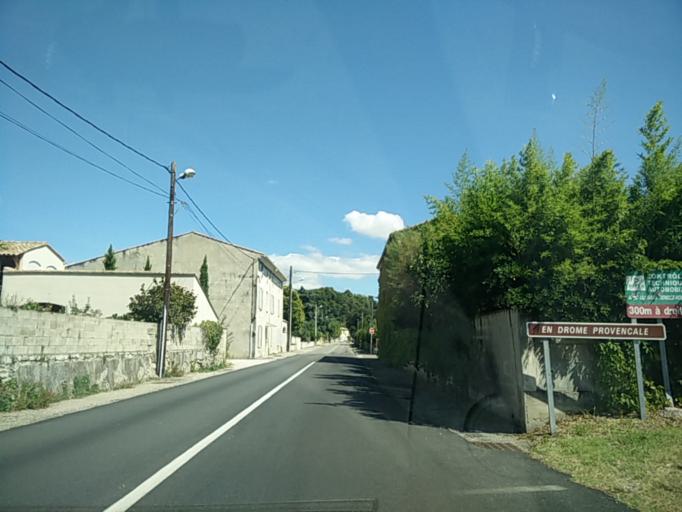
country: FR
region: Rhone-Alpes
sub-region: Departement de la Drome
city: Montboucher-sur-Jabron
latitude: 44.5545
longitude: 4.8584
